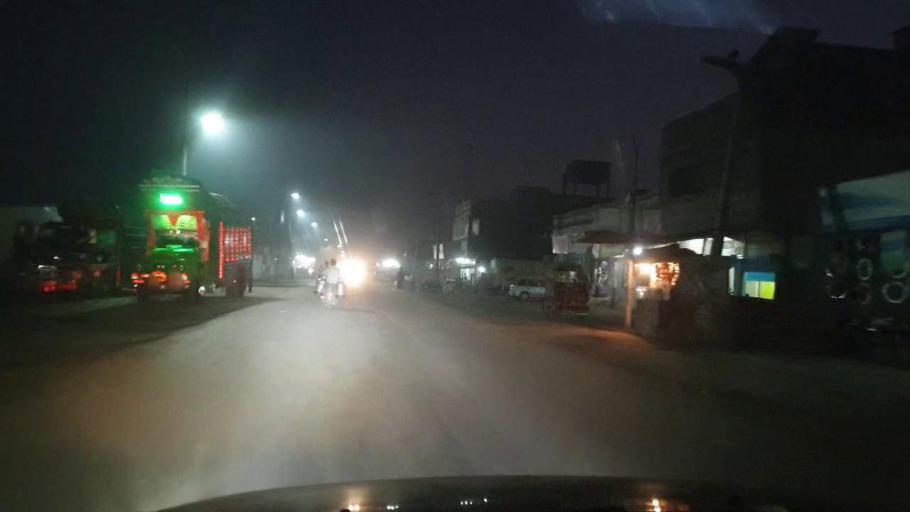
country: PK
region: Sindh
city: Chambar
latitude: 25.2991
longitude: 68.8108
